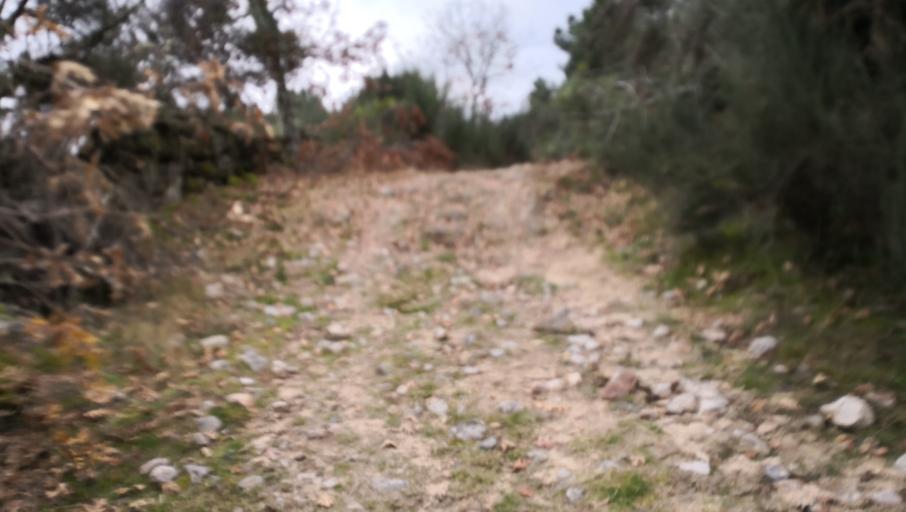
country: PT
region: Vila Real
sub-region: Sabrosa
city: Sabrosa
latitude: 41.3399
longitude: -7.6309
